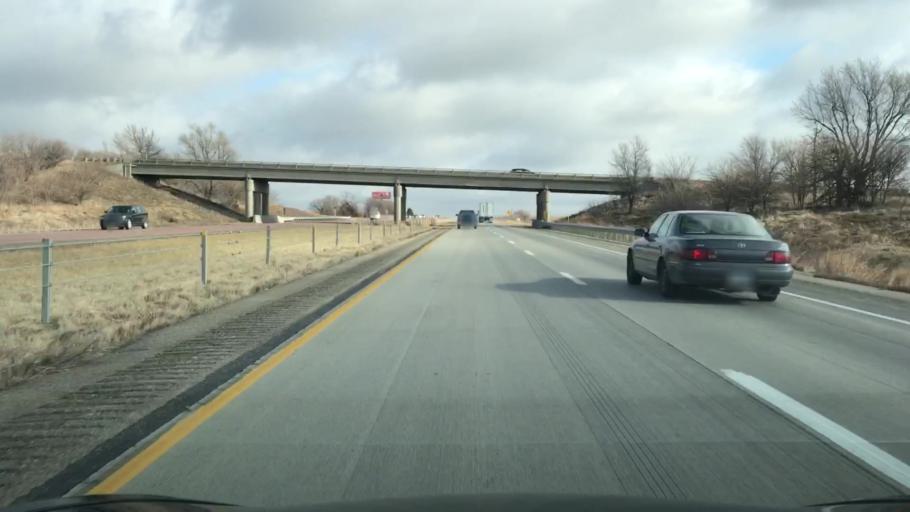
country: US
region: Iowa
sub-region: Guthrie County
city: Guthrie Center
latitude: 41.4930
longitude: -94.6447
